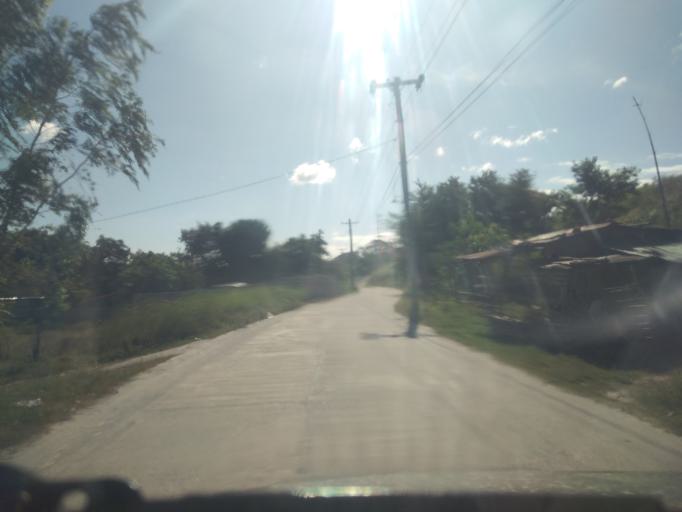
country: PH
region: Central Luzon
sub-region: Province of Pampanga
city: Calibutbut
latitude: 15.0894
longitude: 120.5994
